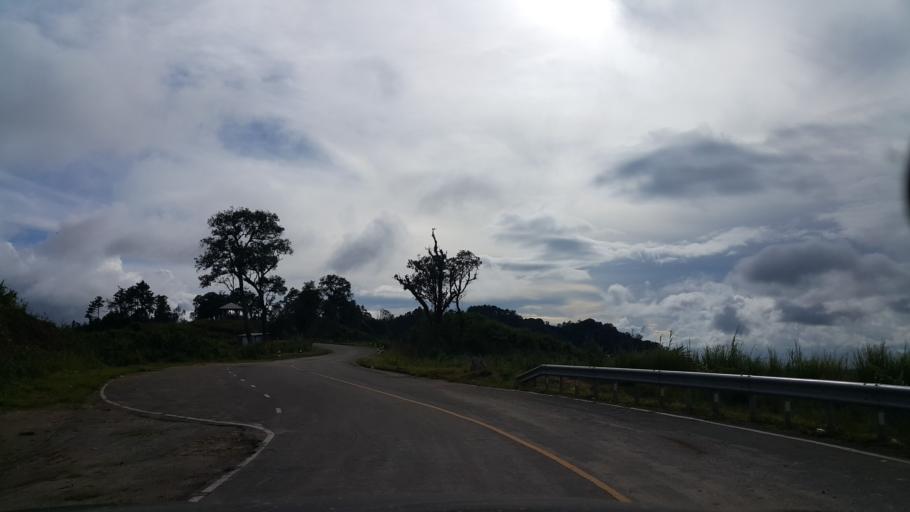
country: TH
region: Chiang Mai
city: Chaem Luang
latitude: 18.9543
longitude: 98.4397
